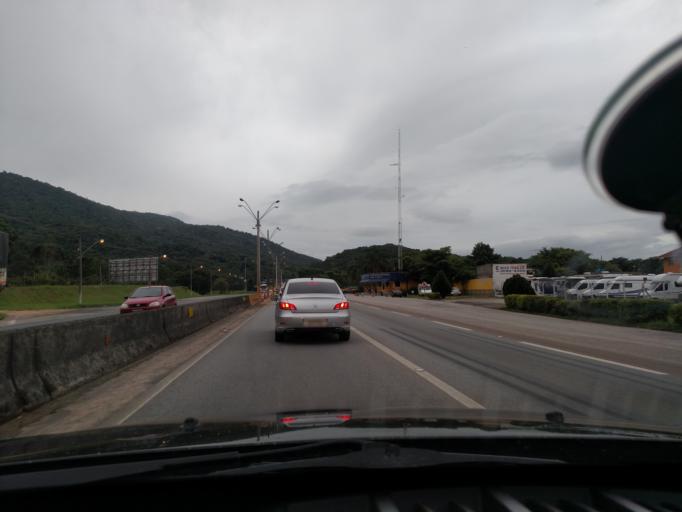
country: BR
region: Santa Catarina
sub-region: Biguacu
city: Biguacu
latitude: -27.4716
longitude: -48.6412
